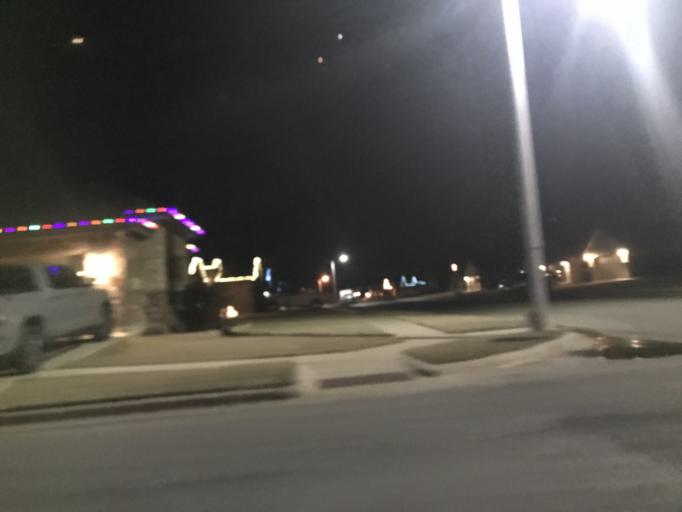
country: US
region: Texas
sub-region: Taylor County
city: Abilene
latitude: 32.3751
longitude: -99.7198
